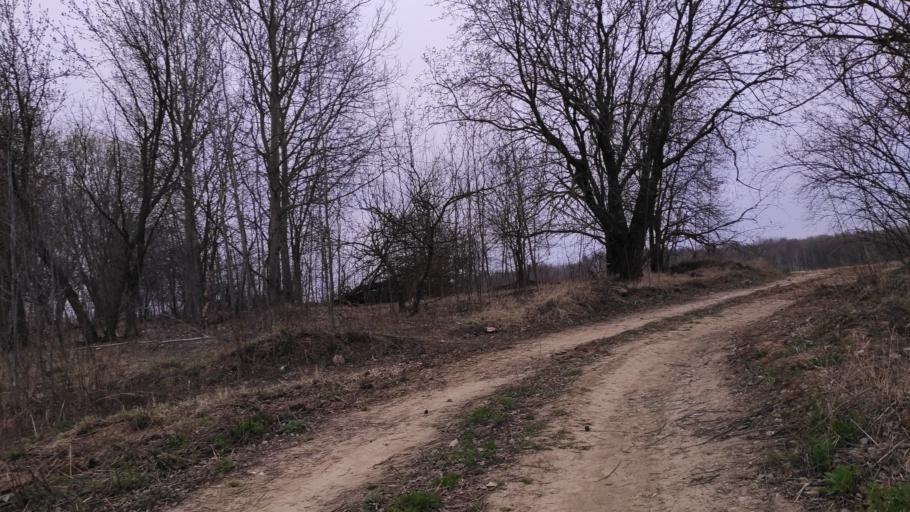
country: BY
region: Minsk
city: Novoye Medvezhino
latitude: 53.8832
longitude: 27.4663
